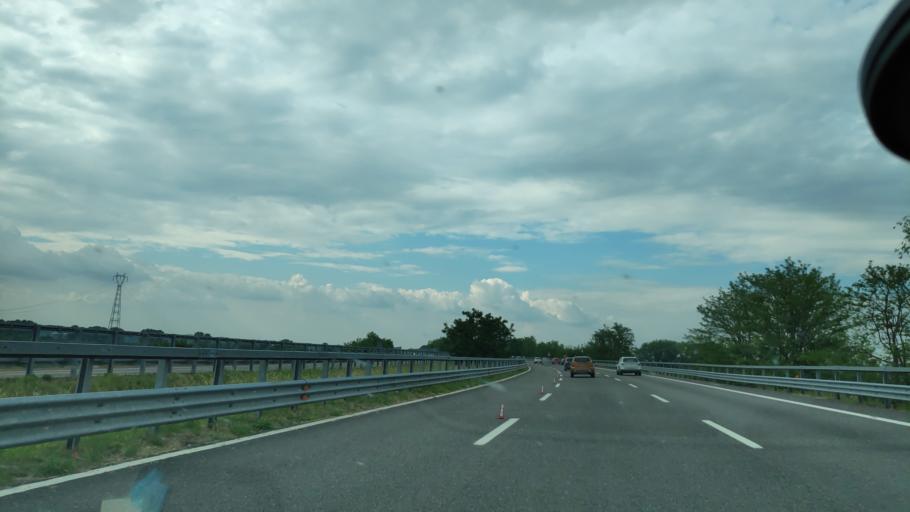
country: IT
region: Lombardy
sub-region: Provincia di Pavia
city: Corana
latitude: 45.0772
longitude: 8.9740
